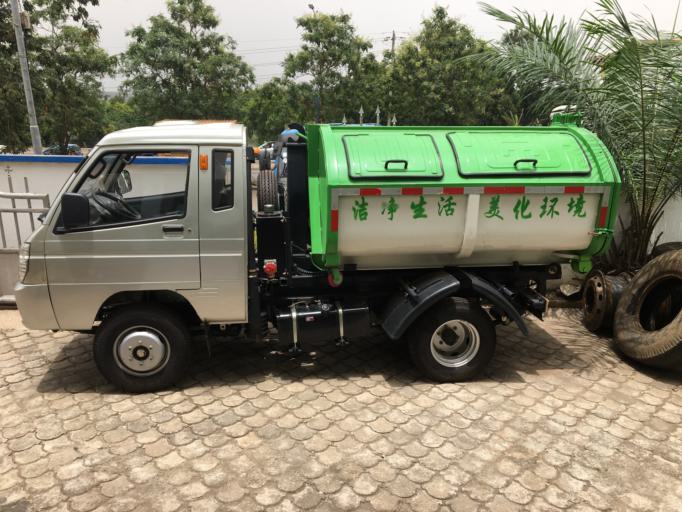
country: GH
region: Greater Accra
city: Accra
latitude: 5.6000
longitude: -0.1965
